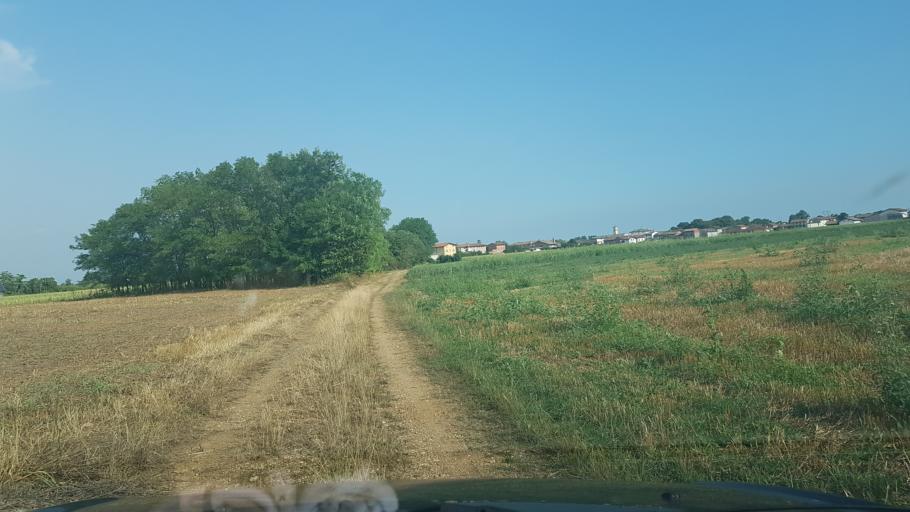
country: IT
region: Friuli Venezia Giulia
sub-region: Provincia di Udine
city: San Vito di Fagagna
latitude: 46.0620
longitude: 13.0801
